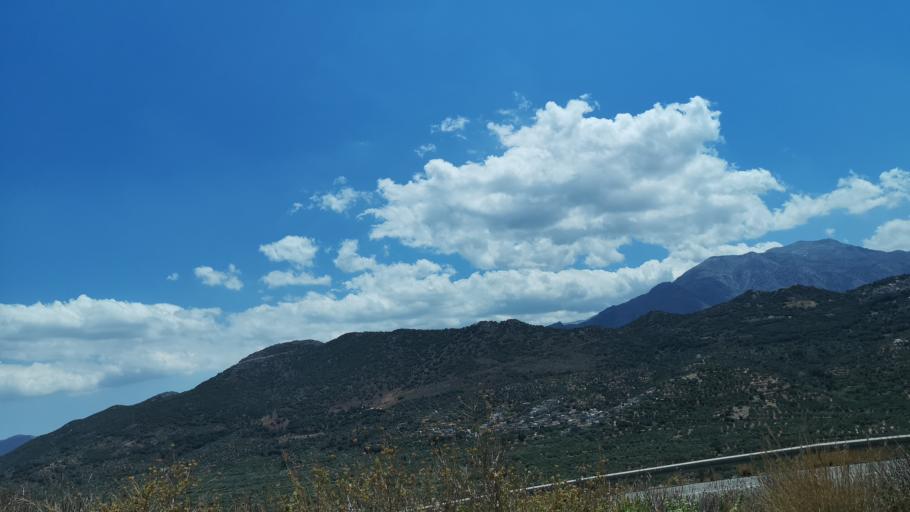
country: GR
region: Crete
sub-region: Nomos Lasithiou
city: Neapoli
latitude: 35.2522
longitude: 25.6308
